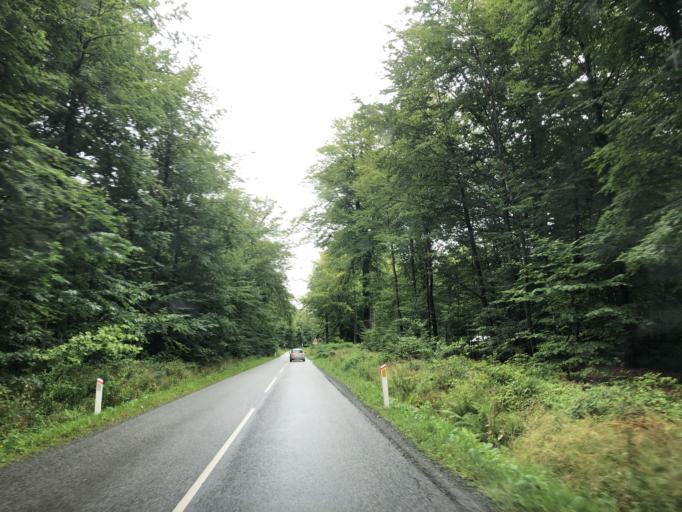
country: DK
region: South Denmark
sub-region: Vejle Kommune
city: Borkop
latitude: 55.6821
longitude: 9.6154
